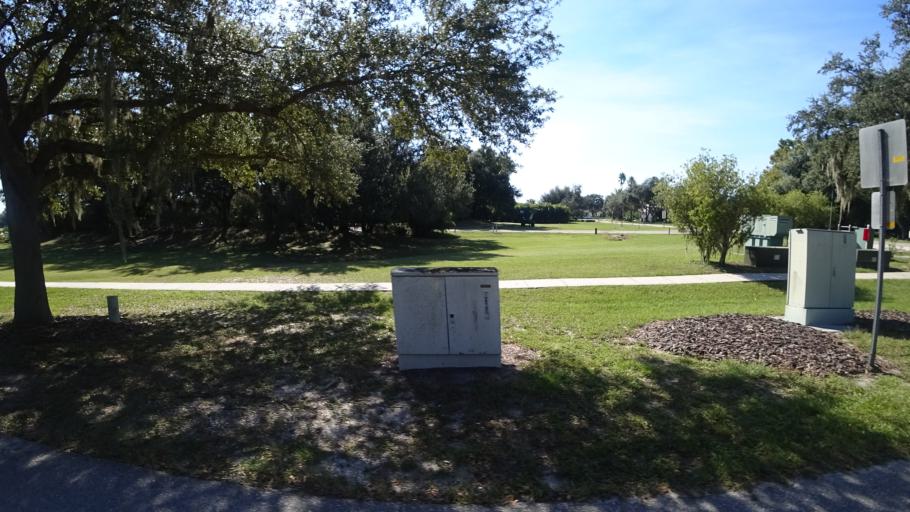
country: US
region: Florida
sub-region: Sarasota County
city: The Meadows
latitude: 27.4278
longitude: -82.4360
